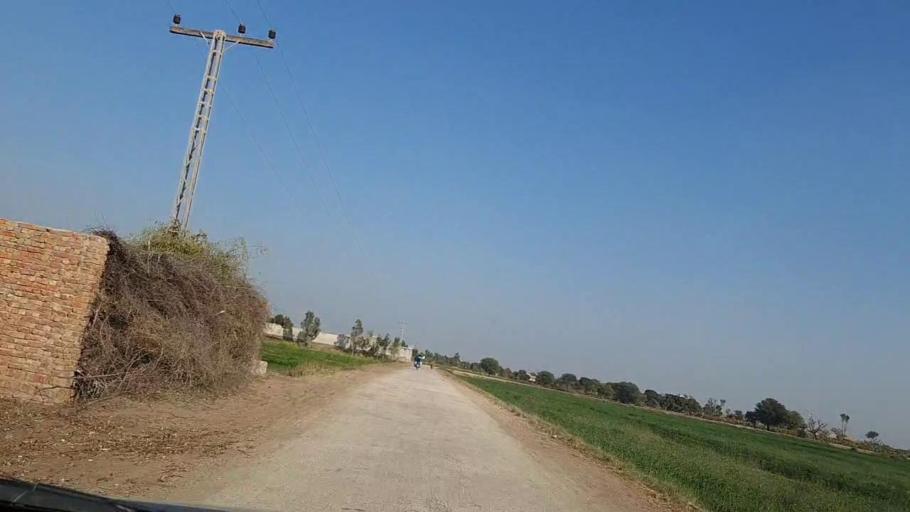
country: PK
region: Sindh
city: Sakrand
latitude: 26.0201
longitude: 68.3383
